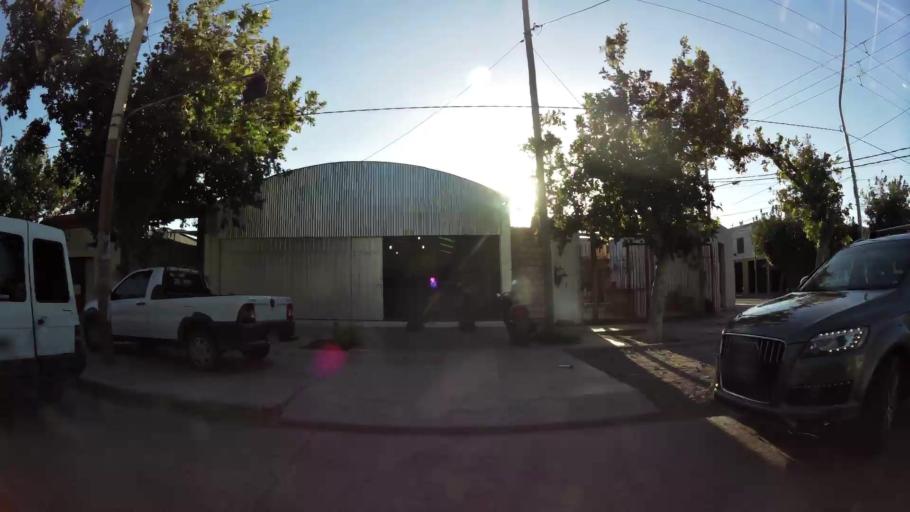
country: AR
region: San Juan
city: Villa Krause
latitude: -31.5527
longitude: -68.5243
